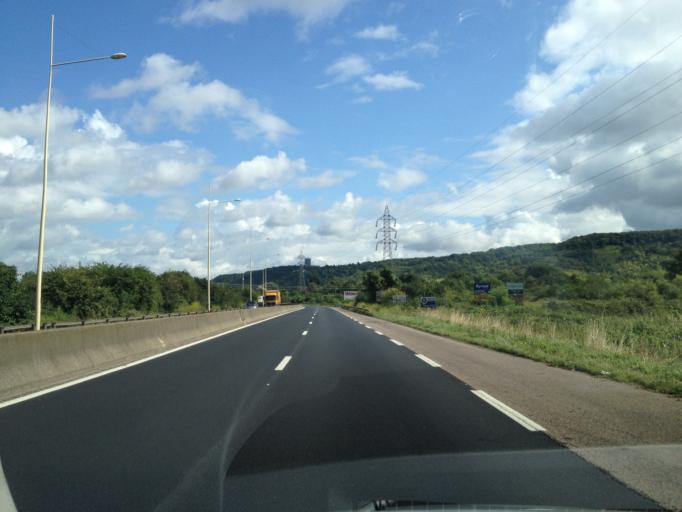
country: FR
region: Haute-Normandie
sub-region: Departement de la Seine-Maritime
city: Saint-Etienne-du-Rouvray
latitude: 49.3698
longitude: 1.1143
